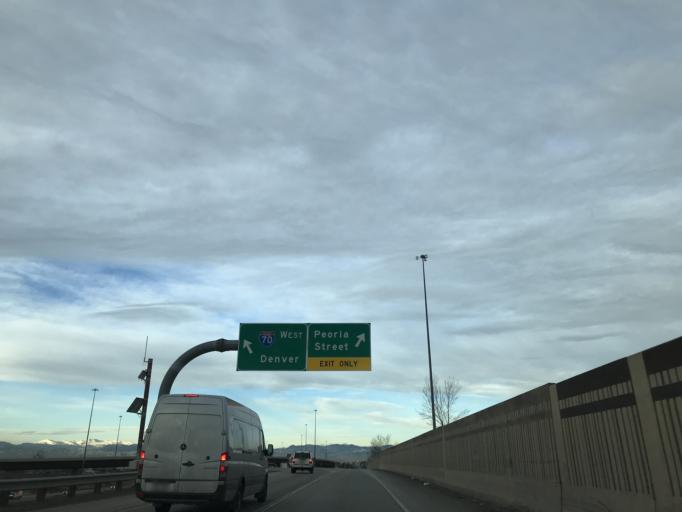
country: US
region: Colorado
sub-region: Adams County
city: Aurora
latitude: 39.7730
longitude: -104.8255
